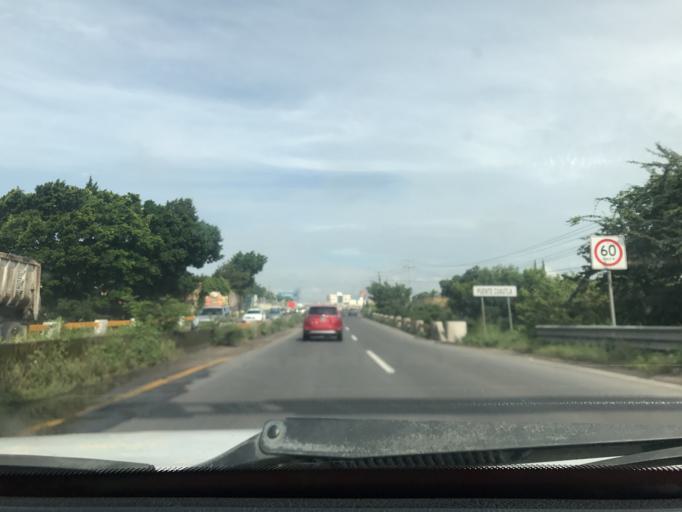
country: MX
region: Morelos
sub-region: Cuautla
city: Tierra Larga (Campo Nuevo)
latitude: 18.8472
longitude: -98.9319
